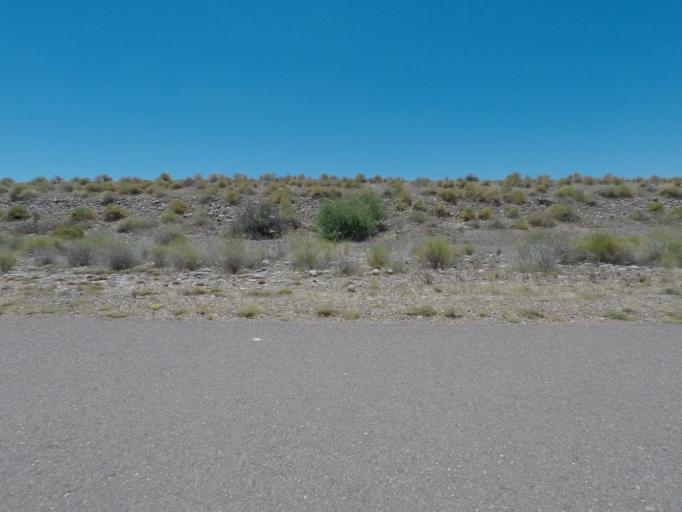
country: US
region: Arizona
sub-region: Maricopa County
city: Phoenix
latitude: 33.4159
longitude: -112.0349
